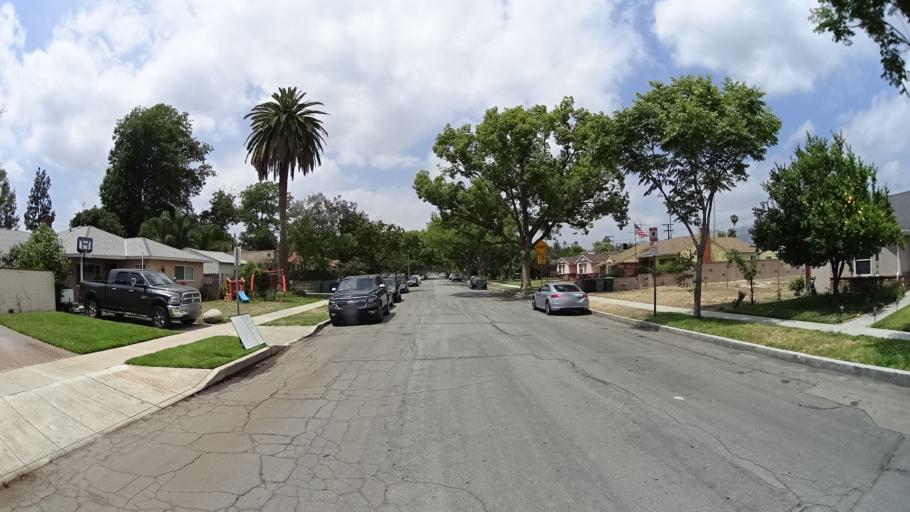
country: US
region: California
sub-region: Los Angeles County
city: Universal City
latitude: 34.1604
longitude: -118.3340
